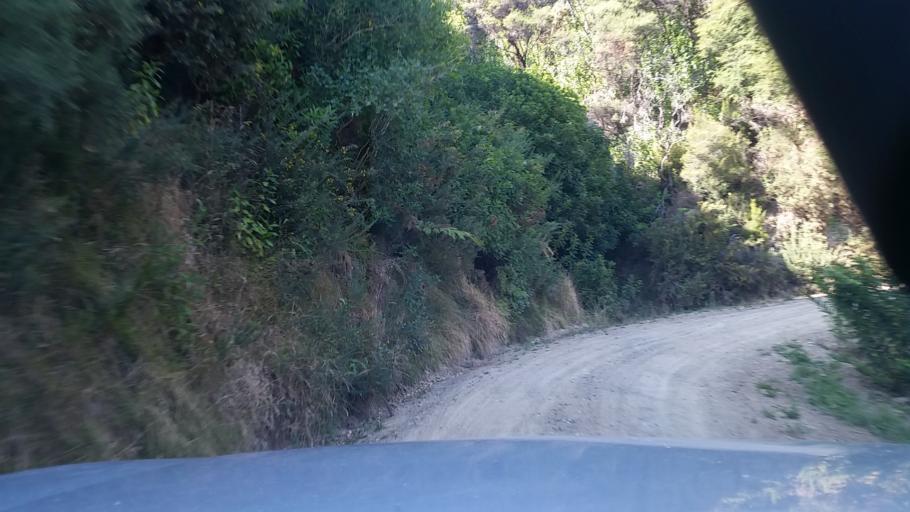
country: NZ
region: Marlborough
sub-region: Marlborough District
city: Picton
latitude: -41.3074
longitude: 174.1732
